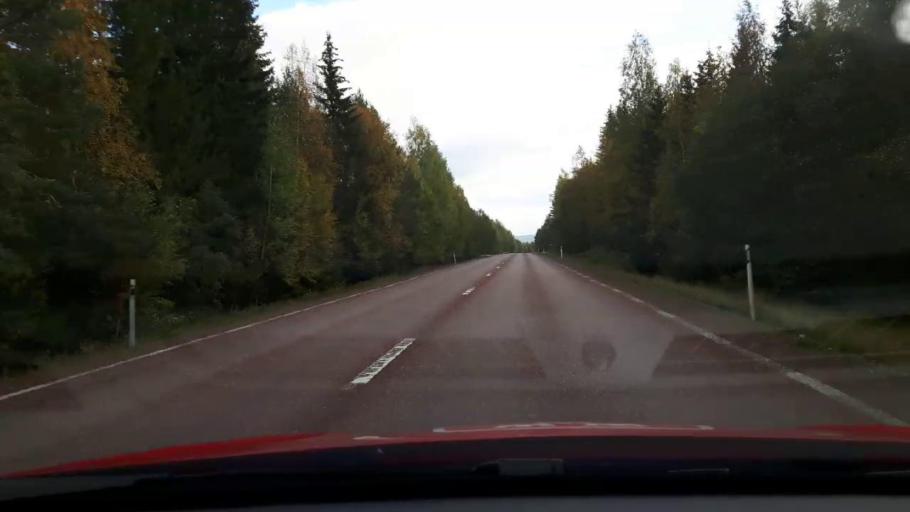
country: SE
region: Gaevleborg
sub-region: Ljusdals Kommun
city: Jaervsoe
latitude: 61.6373
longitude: 16.2488
